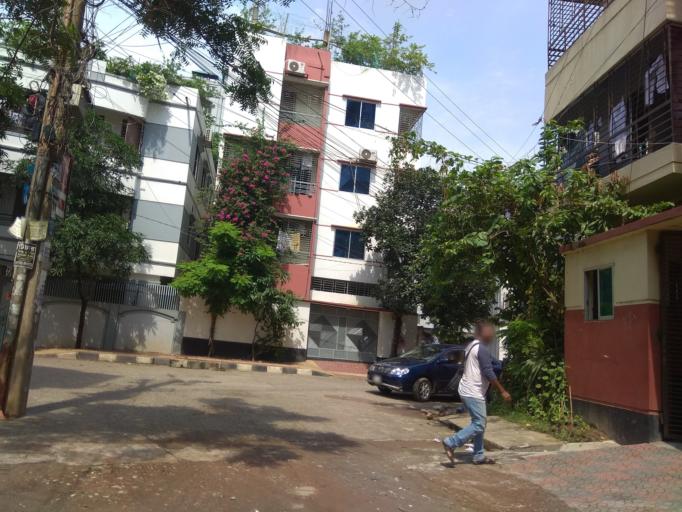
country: BD
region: Dhaka
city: Azimpur
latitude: 23.8090
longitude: 90.3556
